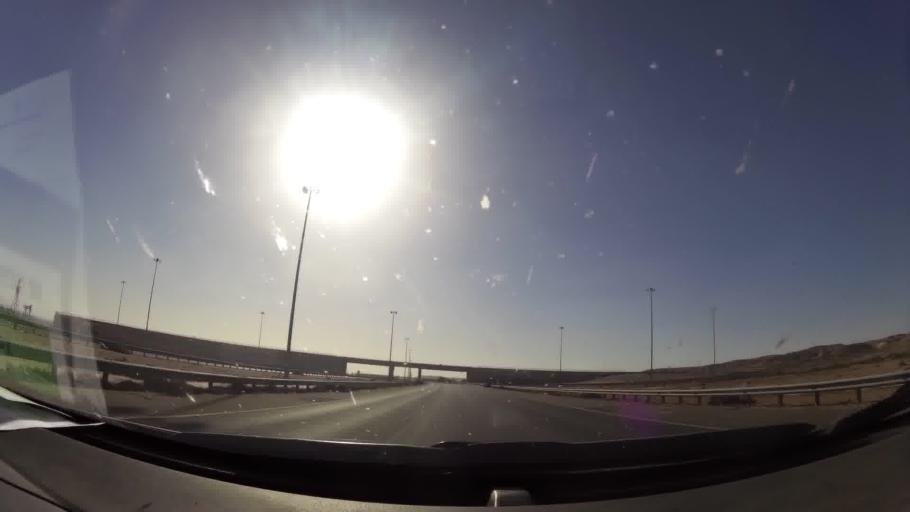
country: KW
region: Al Asimah
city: Kuwait City
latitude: 29.5294
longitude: 47.8239
